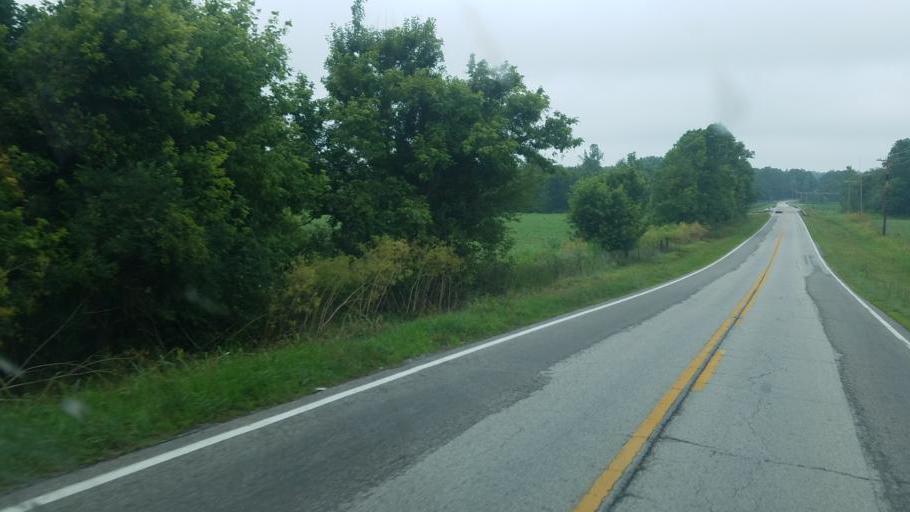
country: US
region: Ohio
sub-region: Highland County
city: Hillsboro
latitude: 39.2334
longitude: -83.5748
